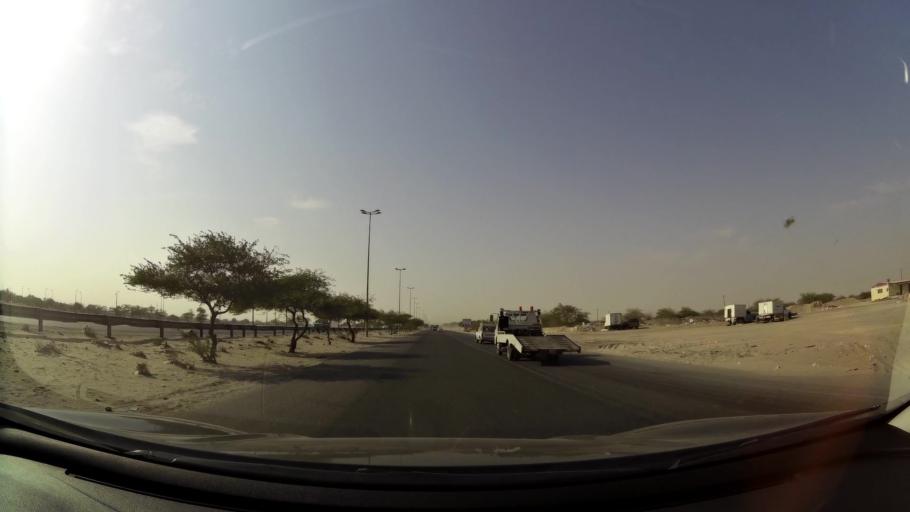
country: KW
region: Al Ahmadi
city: Al Ahmadi
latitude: 28.9491
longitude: 48.1167
